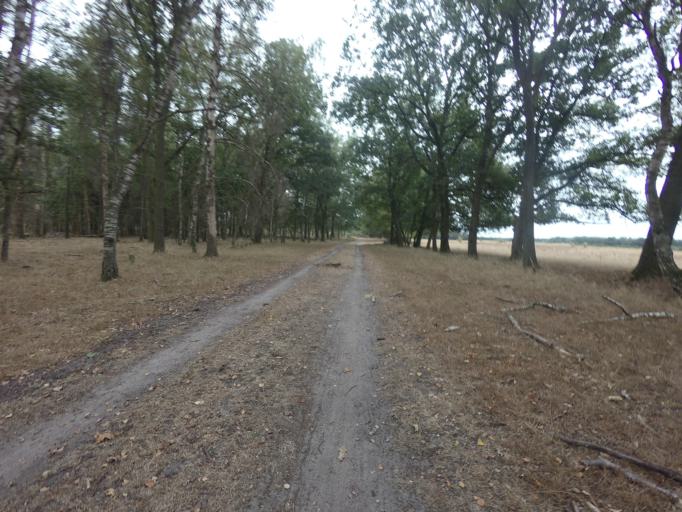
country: NL
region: North Brabant
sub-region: Gemeente Landerd
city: Schaijk
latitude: 51.7086
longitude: 5.6187
